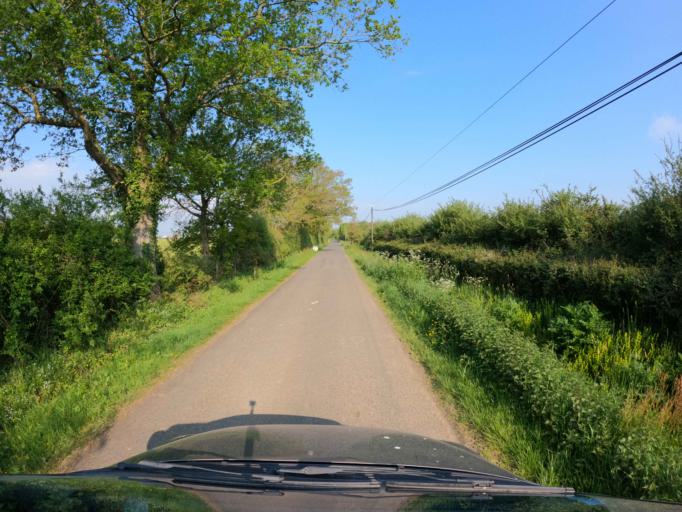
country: FR
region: Pays de la Loire
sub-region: Departement de Maine-et-Loire
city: La Romagne
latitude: 47.0713
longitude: -1.0018
